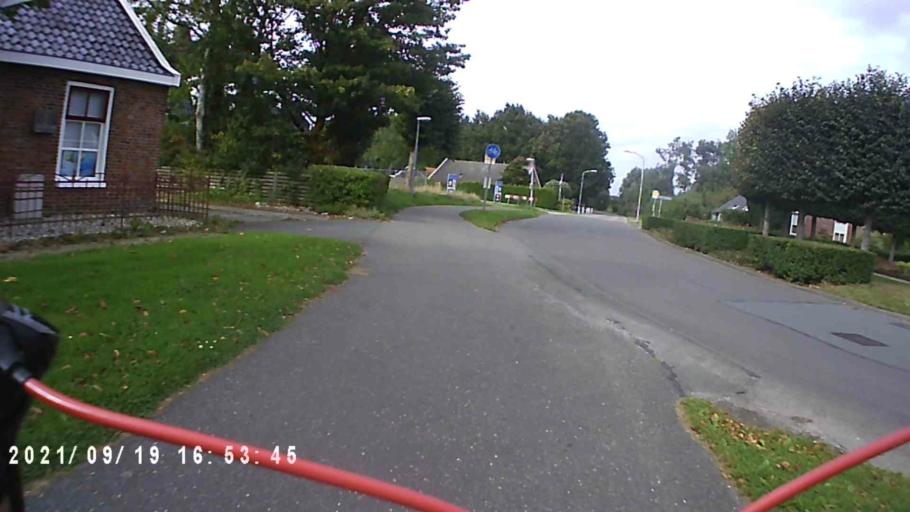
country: NL
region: Groningen
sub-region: Gemeente  Oldambt
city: Winschoten
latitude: 53.1847
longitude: 7.0783
